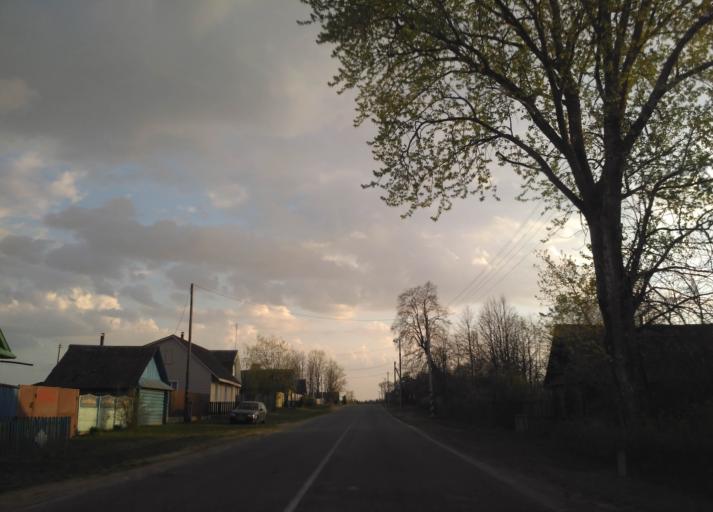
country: BY
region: Minsk
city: Loshnitsa
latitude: 54.4079
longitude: 28.6249
